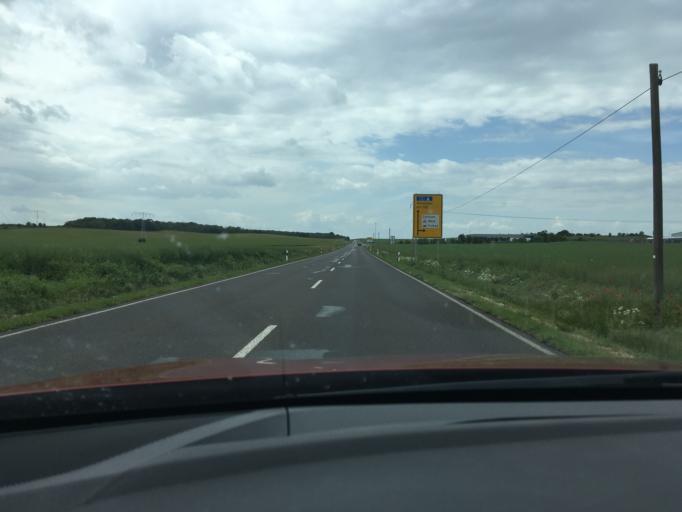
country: DE
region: Saxony-Anhalt
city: Eggersdorf
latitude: 52.0020
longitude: 11.6933
